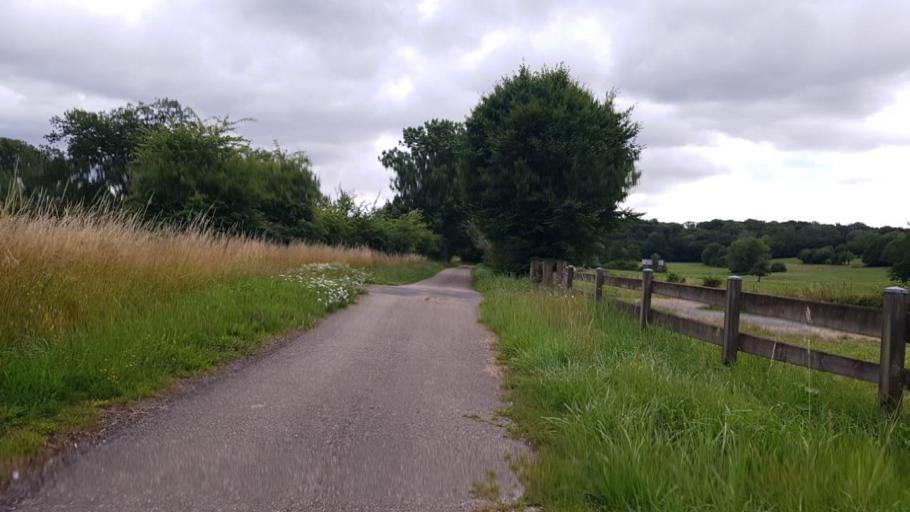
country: FR
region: Picardie
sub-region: Departement de l'Aisne
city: Buironfosse
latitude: 49.9059
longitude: 3.7936
